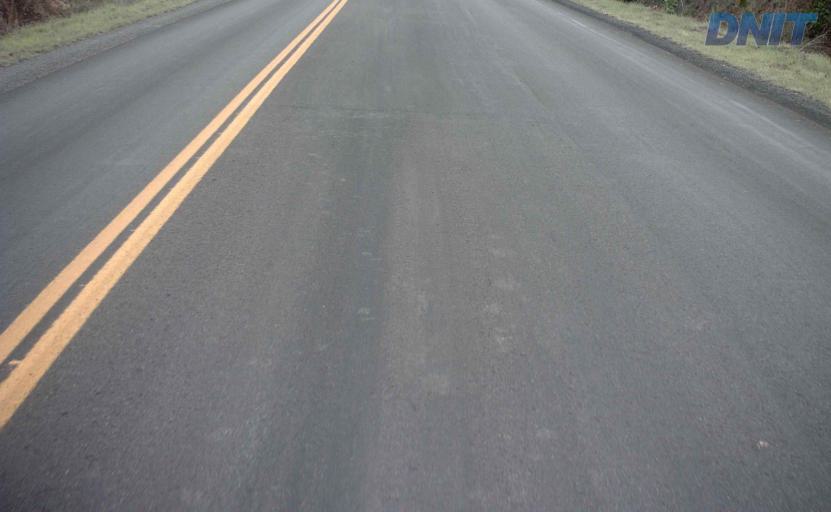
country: BR
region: Goias
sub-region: Padre Bernardo
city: Padre Bernardo
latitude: -15.2114
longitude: -48.5706
